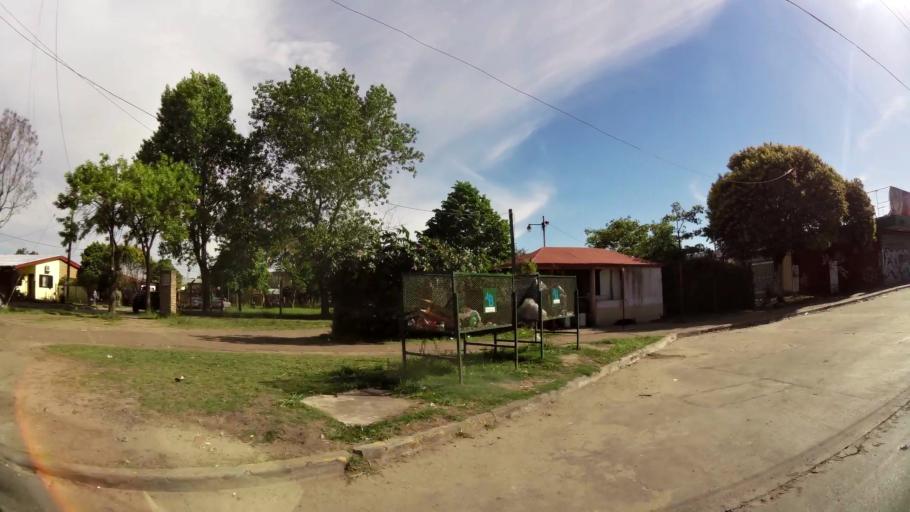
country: AR
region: Buenos Aires
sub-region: Partido de Almirante Brown
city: Adrogue
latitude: -34.8184
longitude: -58.3457
